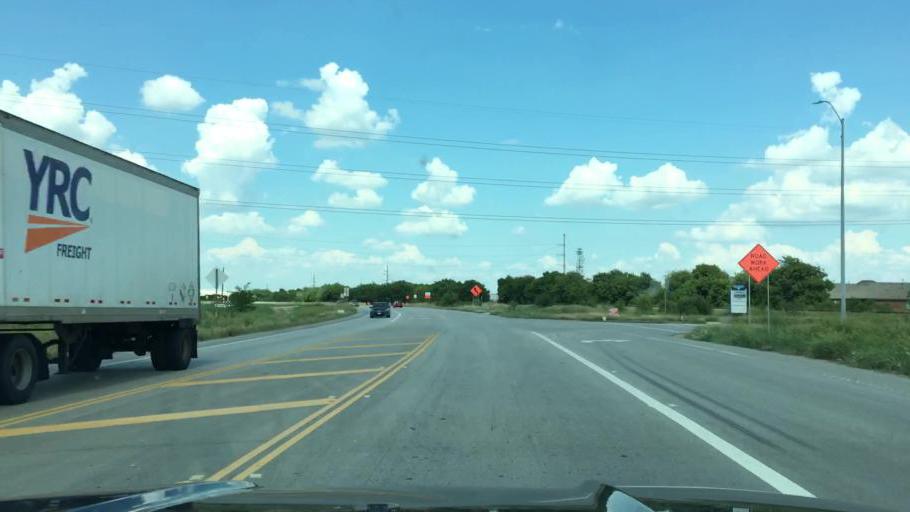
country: US
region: Texas
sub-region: Tarrant County
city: Haslet
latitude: 33.0198
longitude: -97.3131
